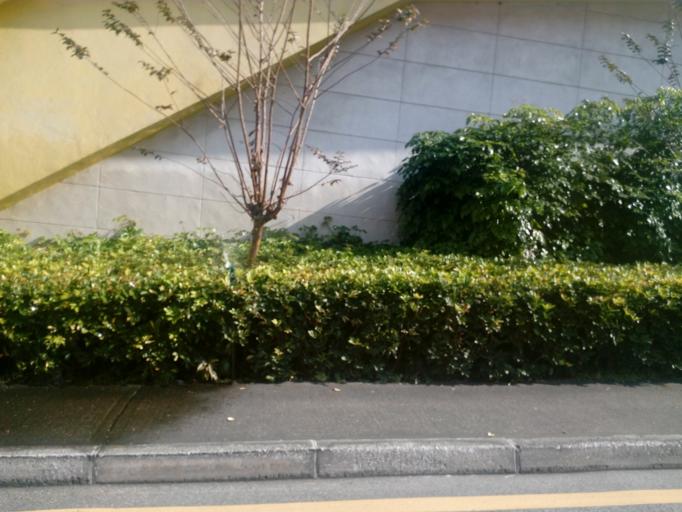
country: MO
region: Macau
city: Macau
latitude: 22.1994
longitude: 113.5502
